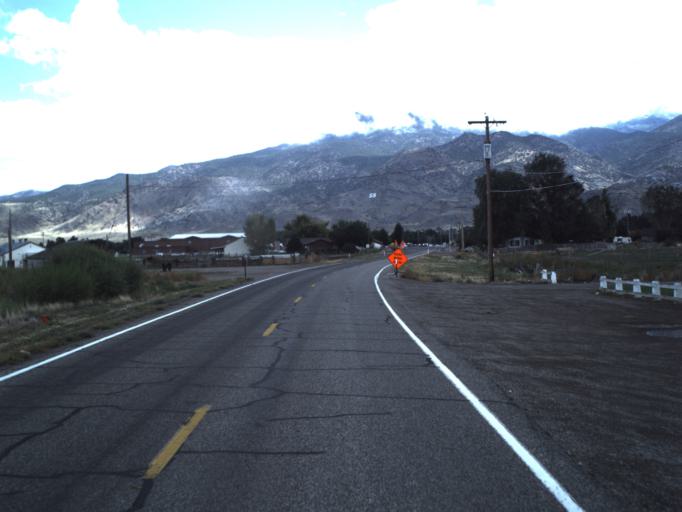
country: US
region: Utah
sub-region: Sevier County
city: Monroe
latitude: 38.6292
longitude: -112.1376
